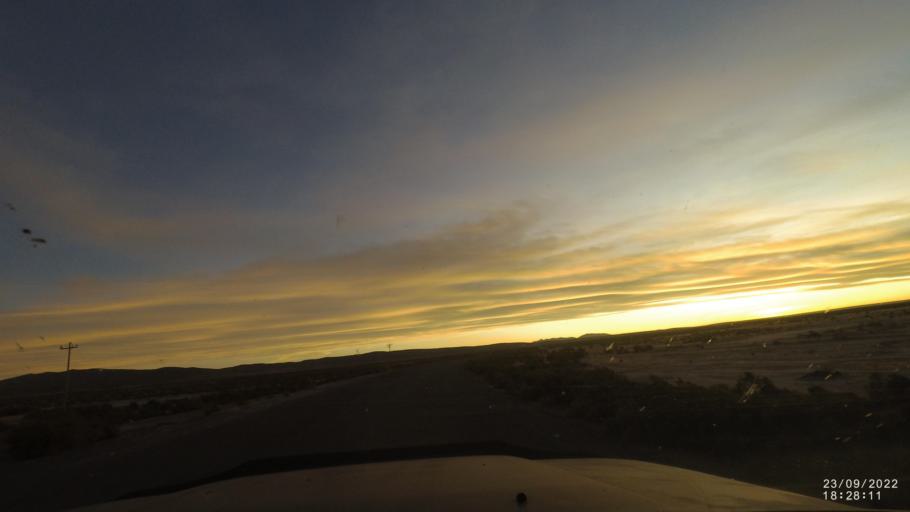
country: BO
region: Oruro
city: Challapata
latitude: -19.3353
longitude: -67.1740
